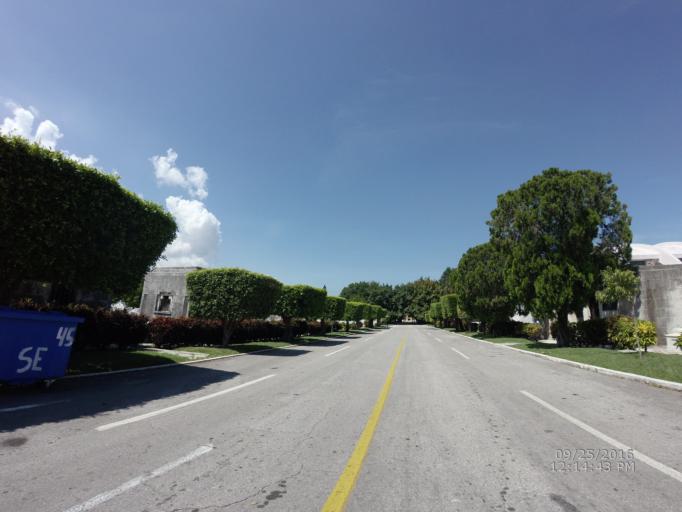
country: CU
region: La Habana
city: Havana
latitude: 23.1229
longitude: -82.3960
